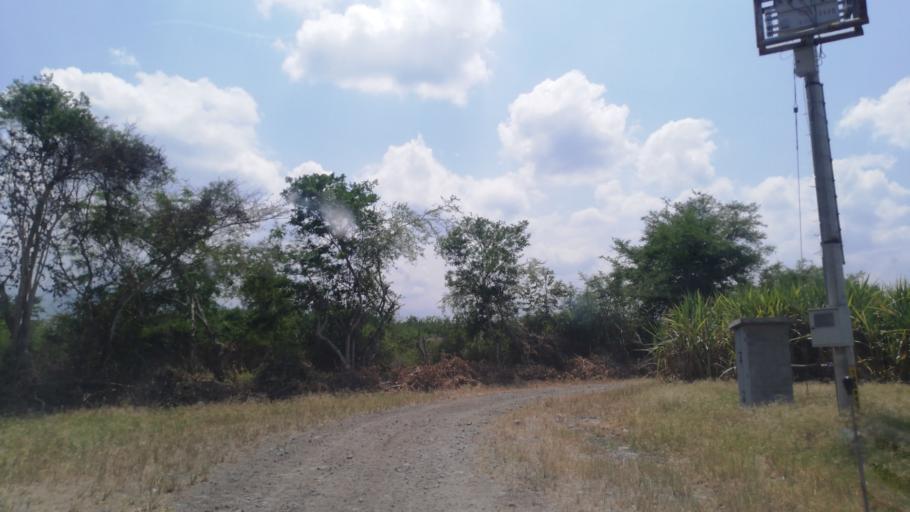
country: CO
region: Valle del Cauca
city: San Pedro
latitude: 3.9874
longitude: -76.2640
